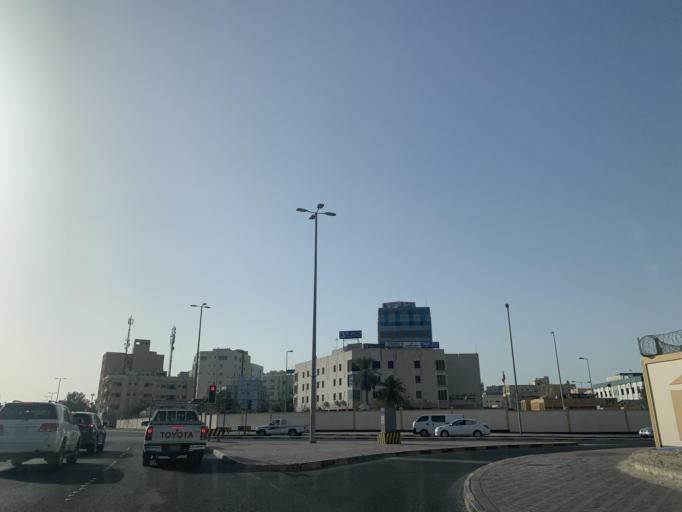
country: BH
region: Manama
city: Manama
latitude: 26.2079
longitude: 50.5951
